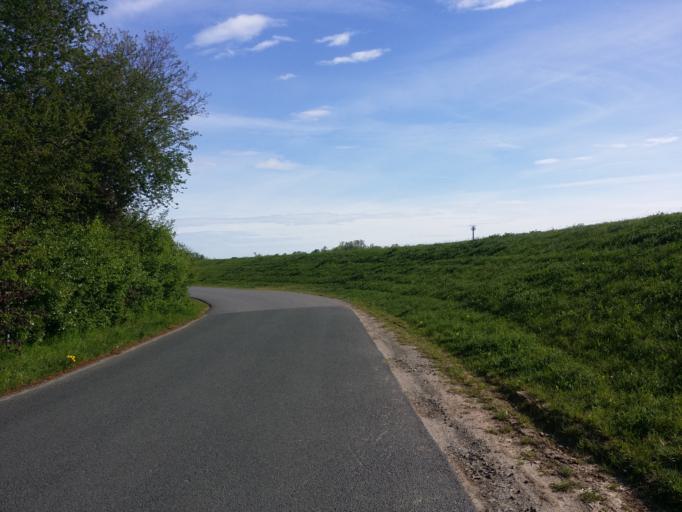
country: DE
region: Lower Saxony
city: Lemwerder
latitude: 53.1330
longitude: 8.6423
